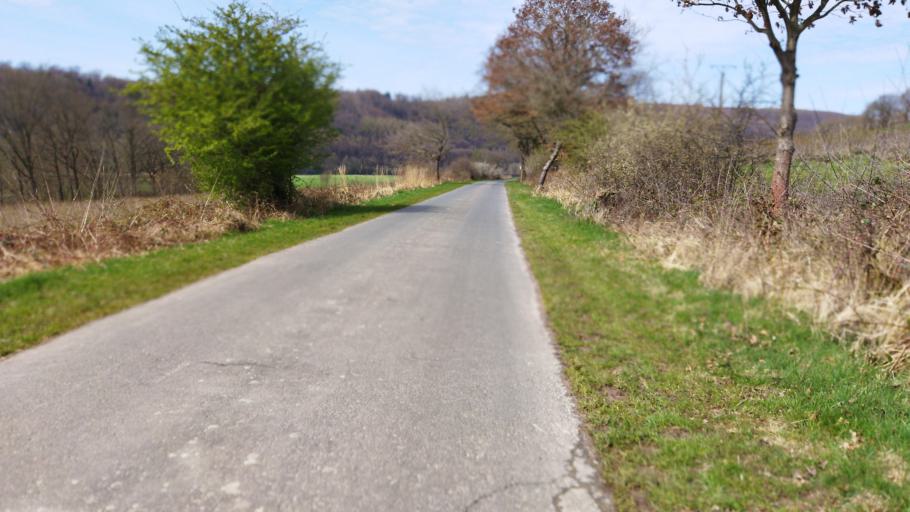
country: DE
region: Lower Saxony
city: Bodenfelde
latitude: 51.6306
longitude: 9.5070
